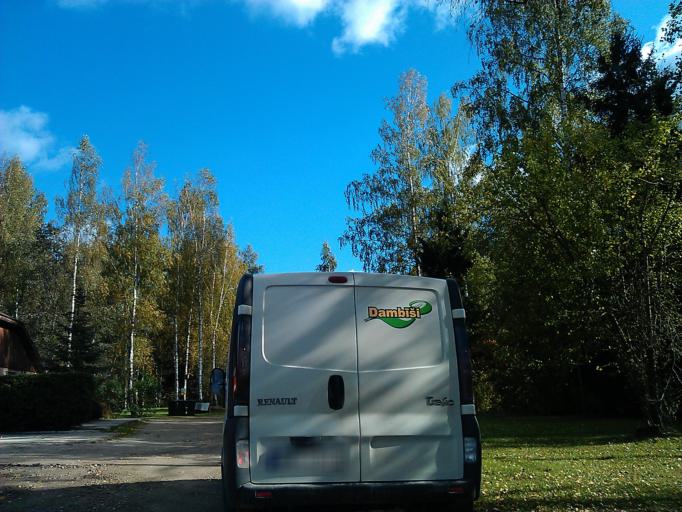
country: LV
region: Livani
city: Livani
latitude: 56.2592
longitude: 26.2074
